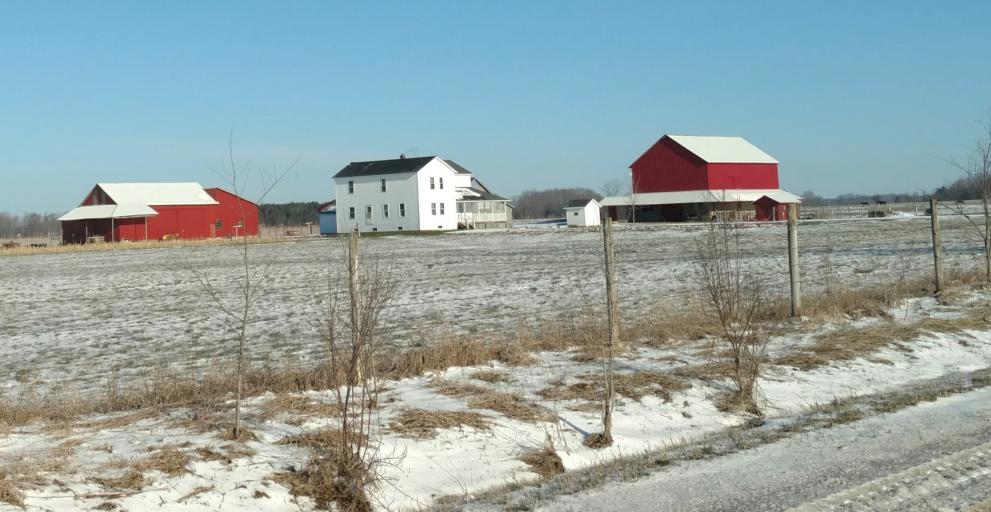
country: US
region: Michigan
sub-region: Gladwin County
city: Gladwin
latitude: 44.0463
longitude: -84.4675
